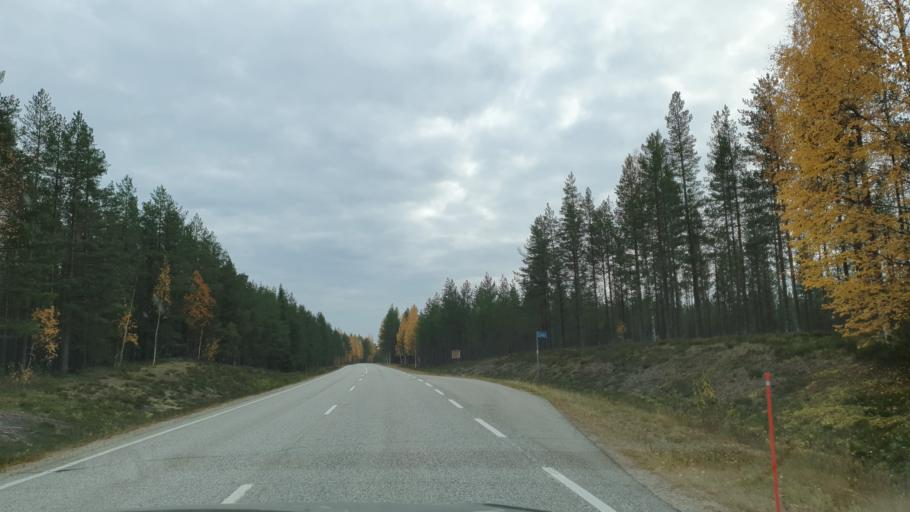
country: FI
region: Kainuu
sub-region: Kehys-Kainuu
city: Puolanka
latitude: 65.2401
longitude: 27.5849
